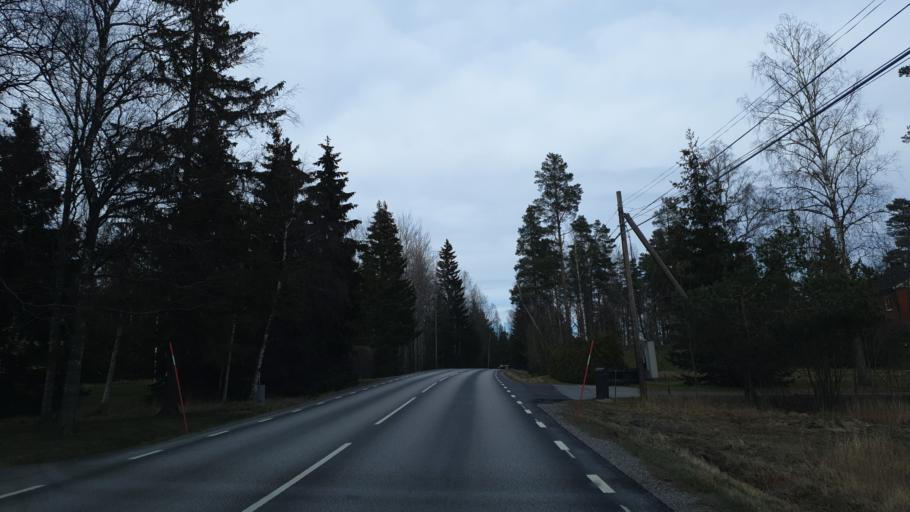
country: SE
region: Stockholm
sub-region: Osterakers Kommun
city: Akersberga
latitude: 59.5782
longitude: 18.2809
